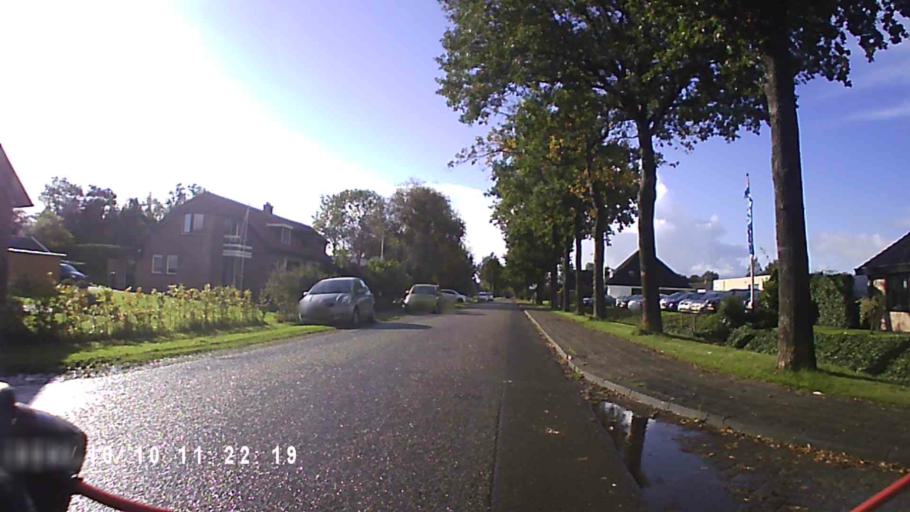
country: NL
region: Friesland
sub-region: Gemeente Smallingerland
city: Drachtstercompagnie
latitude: 53.0935
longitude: 6.1784
